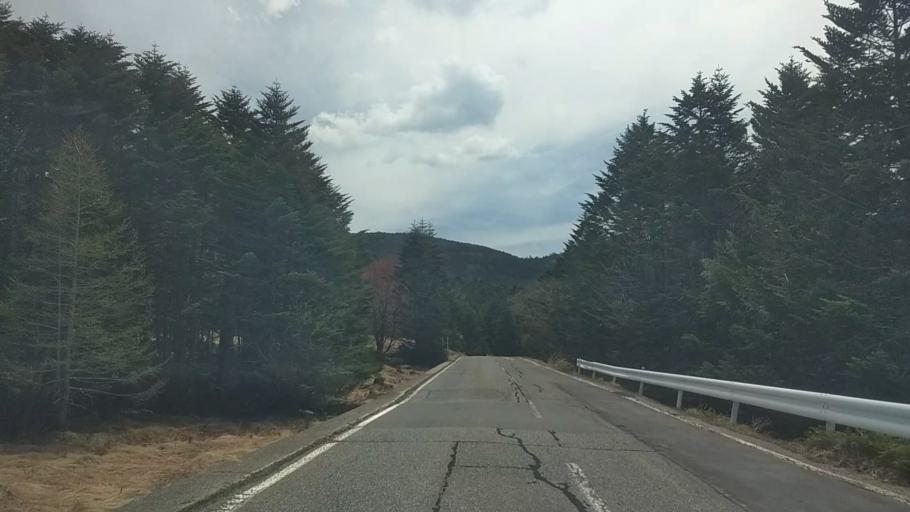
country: JP
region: Nagano
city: Chino
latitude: 36.0581
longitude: 138.3274
